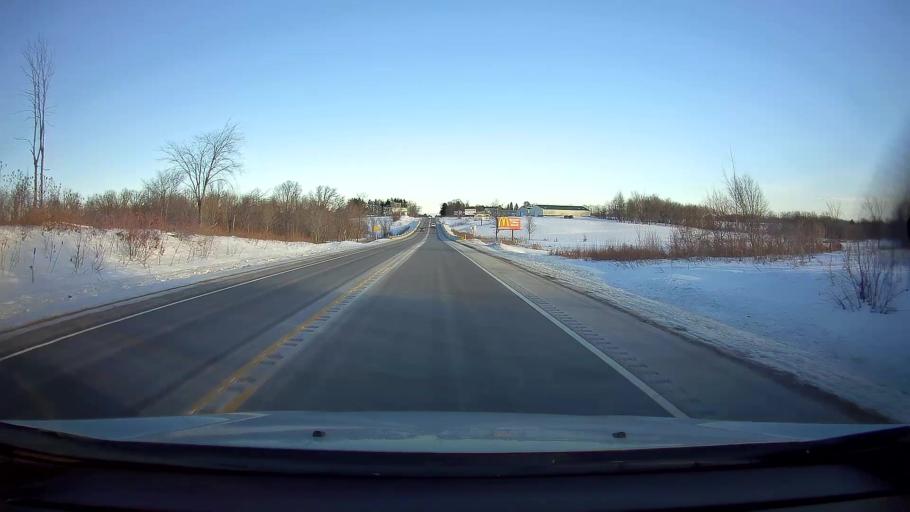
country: US
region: Wisconsin
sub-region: Washburn County
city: Shell Lake
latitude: 45.7664
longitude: -91.9119
